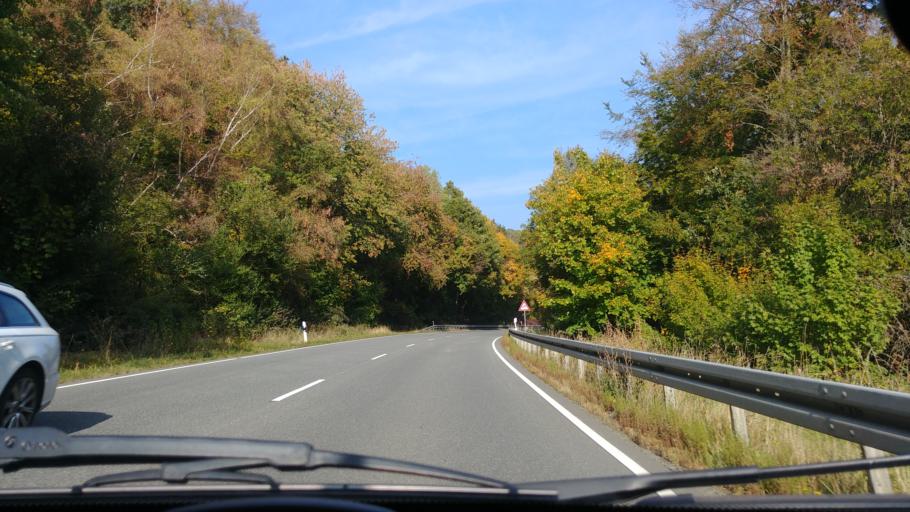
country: DE
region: Hesse
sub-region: Regierungsbezirk Darmstadt
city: Niedernhausen
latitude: 50.1373
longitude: 8.2918
